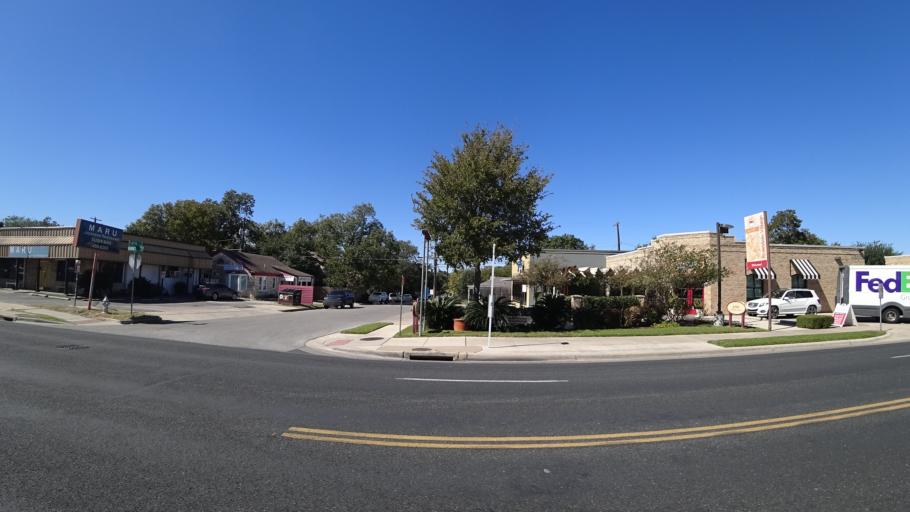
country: US
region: Texas
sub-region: Travis County
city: Austin
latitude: 30.3181
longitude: -97.7399
